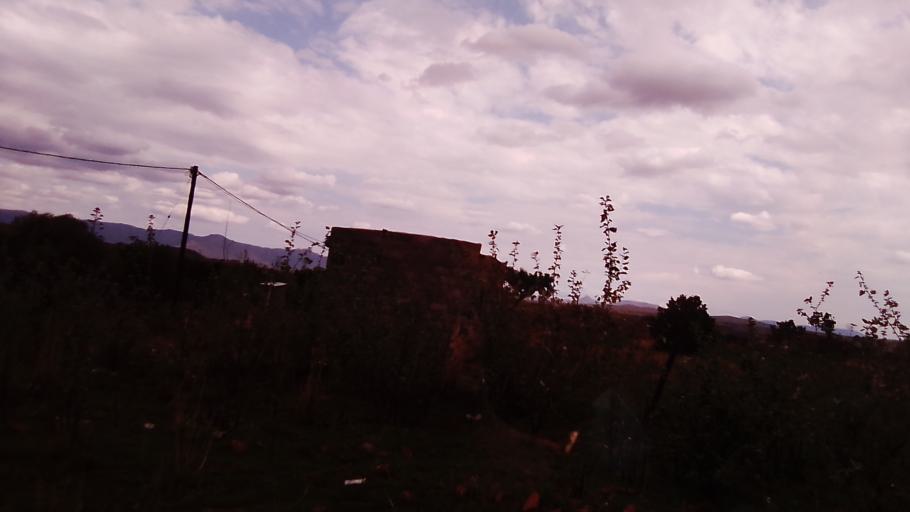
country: LS
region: Berea
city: Teyateyaneng
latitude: -29.3342
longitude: 27.7037
